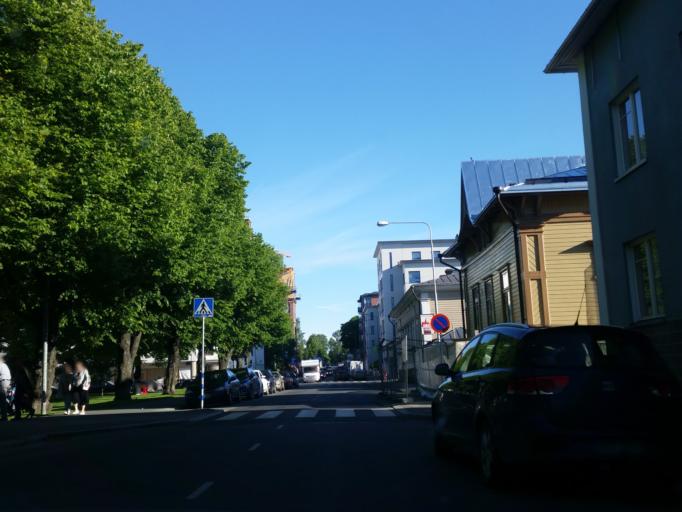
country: FI
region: Northern Savo
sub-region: Kuopio
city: Kuopio
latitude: 62.8920
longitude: 27.6930
